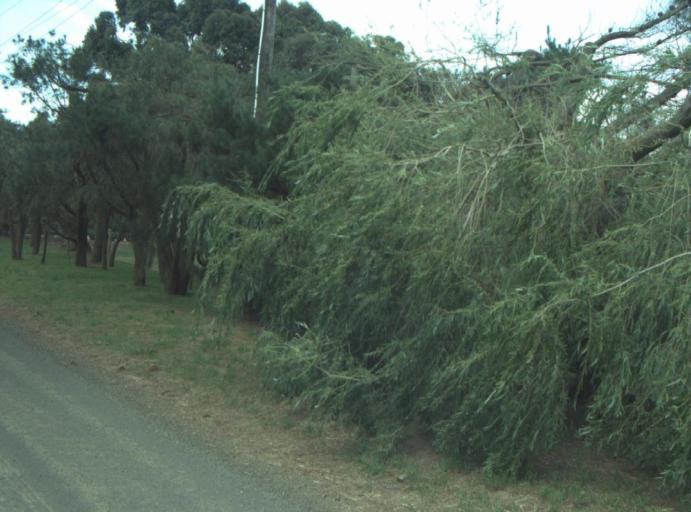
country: AU
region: Victoria
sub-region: Greater Geelong
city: Clifton Springs
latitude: -38.1999
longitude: 144.5656
